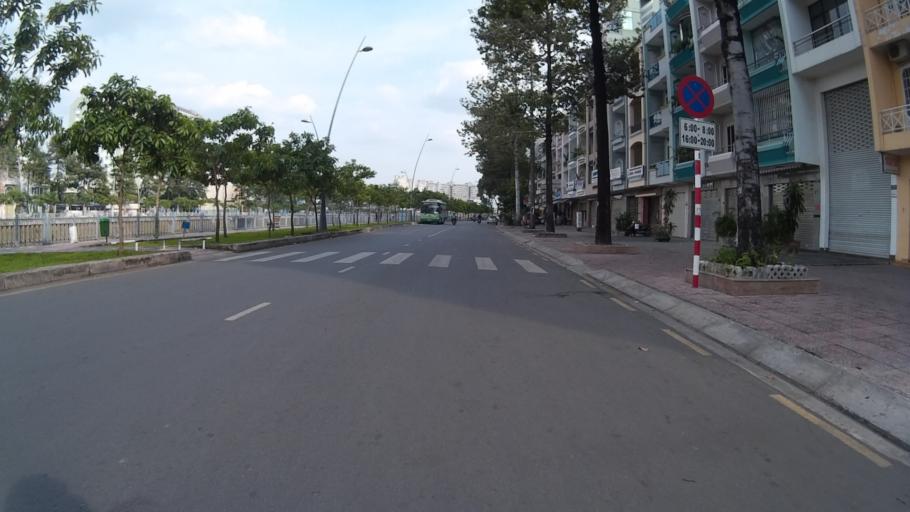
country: VN
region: Ho Chi Minh City
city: Quan Mot
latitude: 10.7923
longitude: 106.7035
